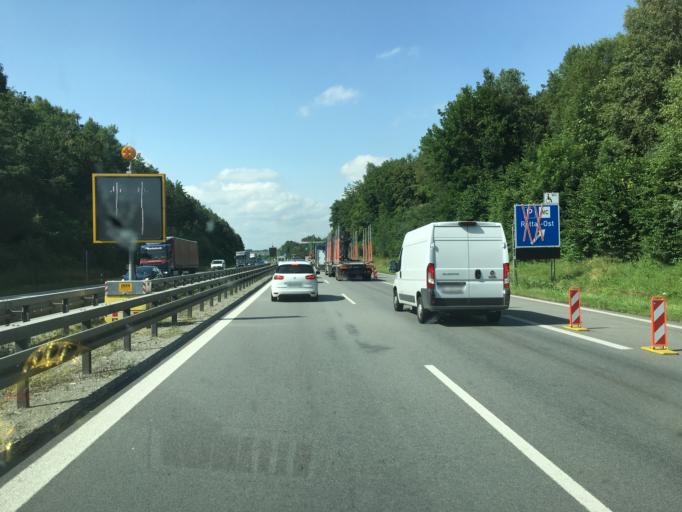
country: AT
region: Upper Austria
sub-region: Politischer Bezirk Scharding
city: Scharding
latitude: 48.4577
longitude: 13.3756
